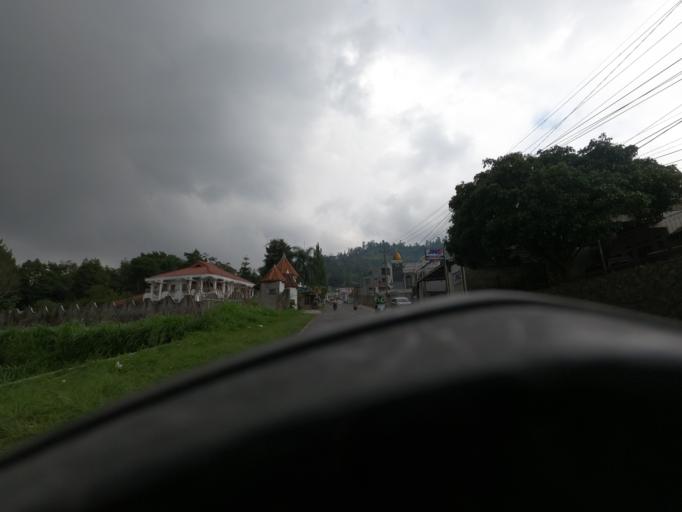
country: ID
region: West Java
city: Lembang
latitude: -6.8077
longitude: 107.6402
